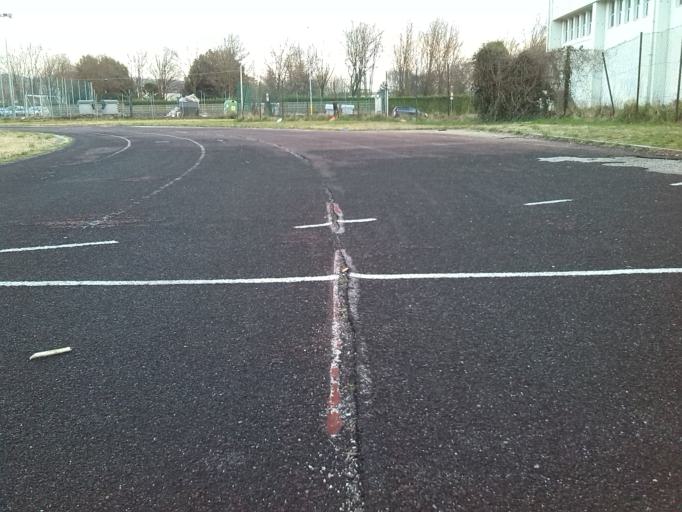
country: IT
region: Friuli Venezia Giulia
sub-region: Provincia di Udine
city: Cividale del Friuli
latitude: 46.0976
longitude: 13.4199
